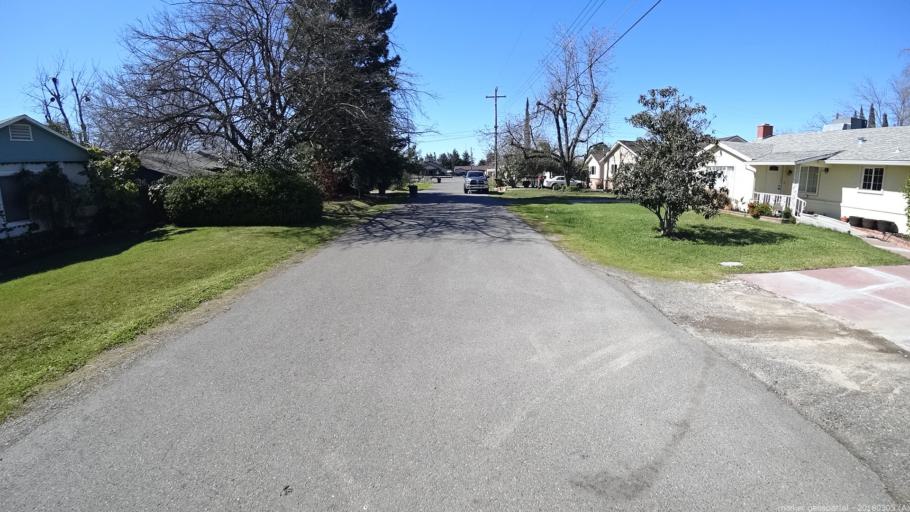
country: US
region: California
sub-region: Sacramento County
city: Florin
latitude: 38.4971
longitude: -121.3892
